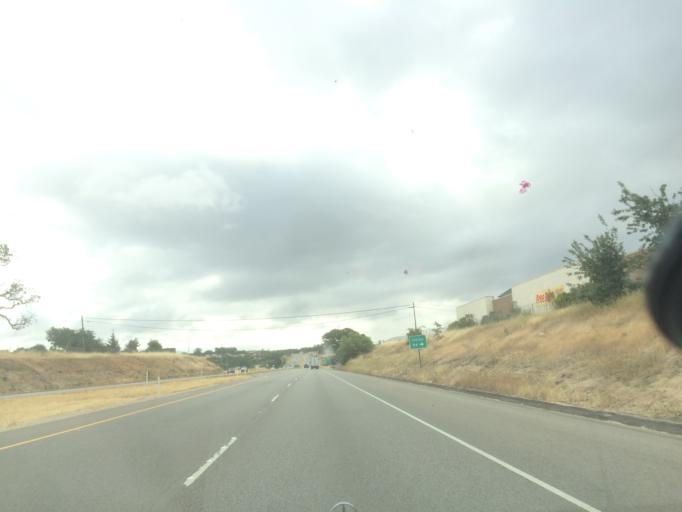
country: US
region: California
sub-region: San Luis Obispo County
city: Paso Robles
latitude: 35.6444
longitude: -120.6526
